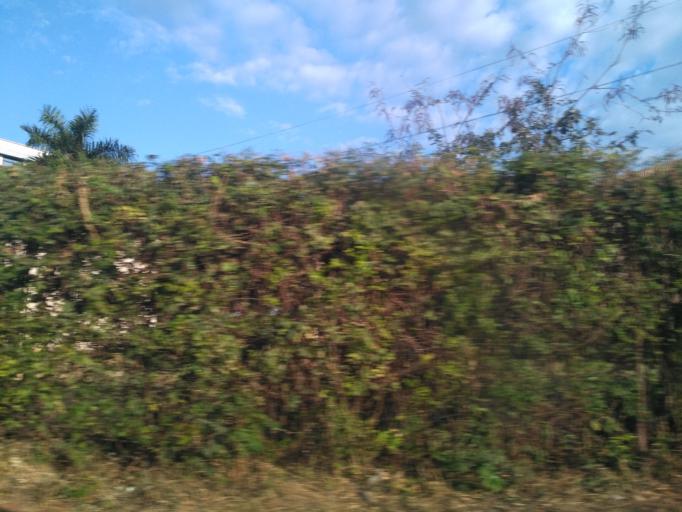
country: TZ
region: Dar es Salaam
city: Magomeni
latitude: -6.7830
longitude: 39.2747
